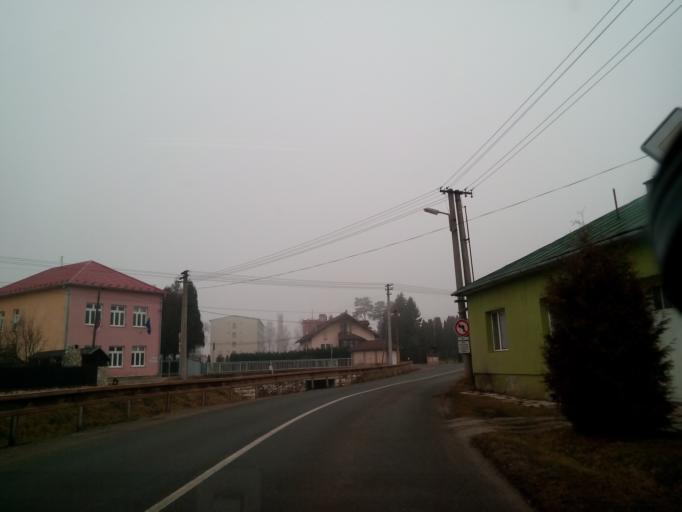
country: SK
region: Presovsky
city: Spisske Podhradie
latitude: 48.9521
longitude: 20.7941
